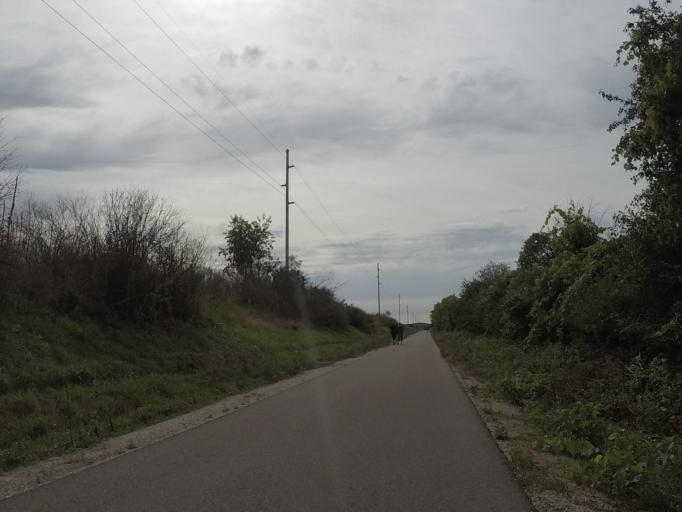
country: US
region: Wisconsin
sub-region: Sauk County
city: Prairie du Sac
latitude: 43.3253
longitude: -89.7460
